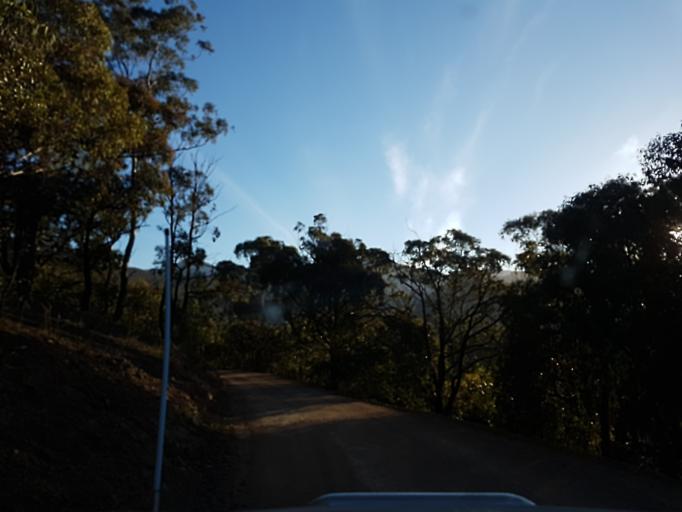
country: AU
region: Victoria
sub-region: Wellington
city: Heyfield
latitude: -37.4028
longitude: 147.0964
